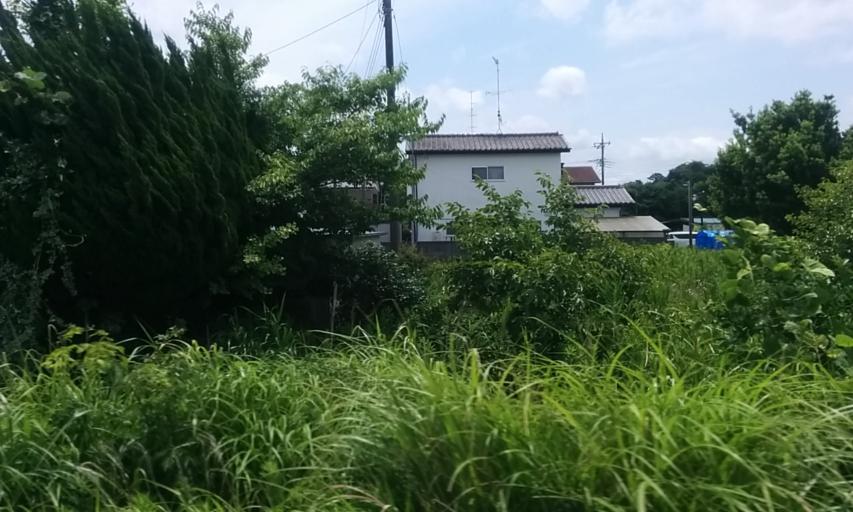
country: JP
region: Ibaraki
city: Edosaki
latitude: 35.8757
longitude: 140.3466
